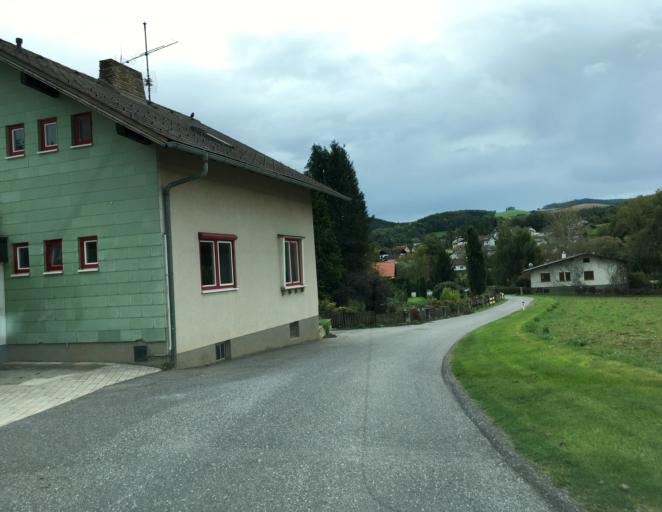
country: AT
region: Lower Austria
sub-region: Politischer Bezirk Wiener Neustadt
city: Bad Schonau
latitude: 47.4985
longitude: 16.2265
